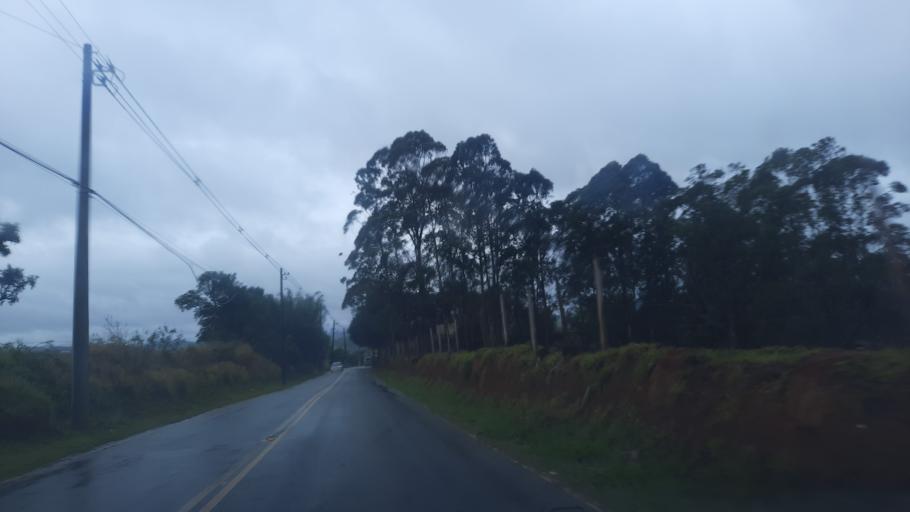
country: BR
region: Sao Paulo
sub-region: Atibaia
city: Atibaia
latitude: -23.0722
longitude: -46.5173
